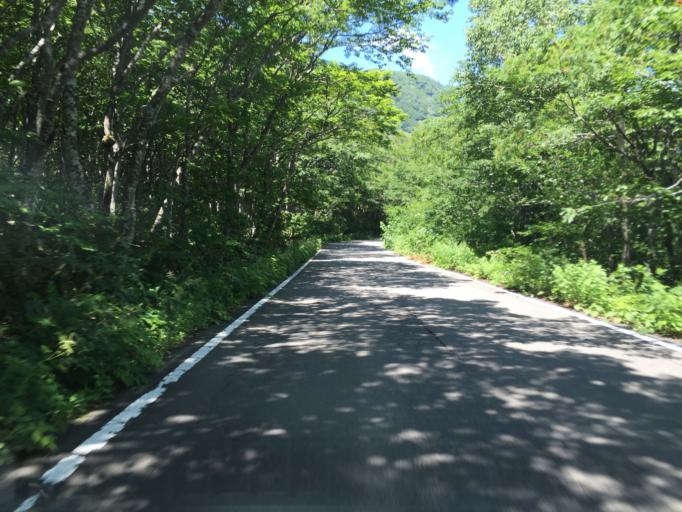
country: JP
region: Fukushima
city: Nihommatsu
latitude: 37.6578
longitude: 140.2887
